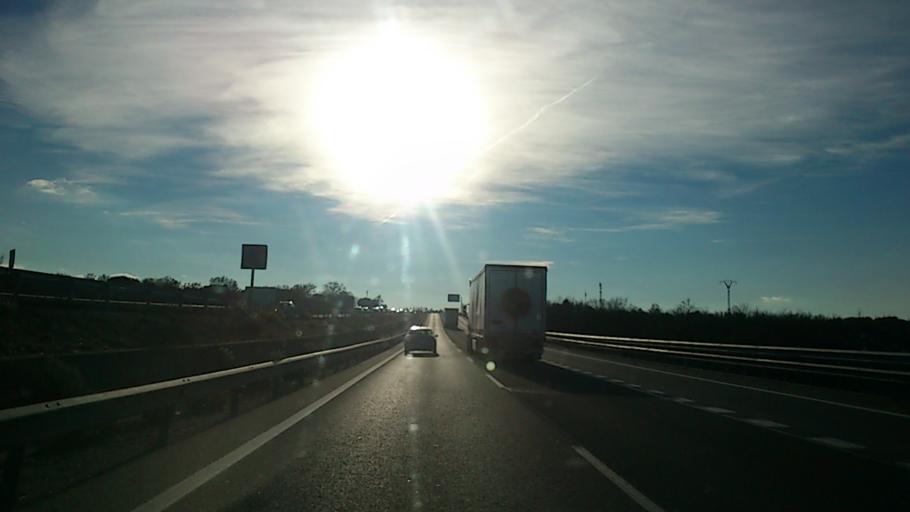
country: ES
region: Castille-La Mancha
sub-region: Provincia de Guadalajara
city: Almadrones
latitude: 40.9069
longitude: -2.7458
